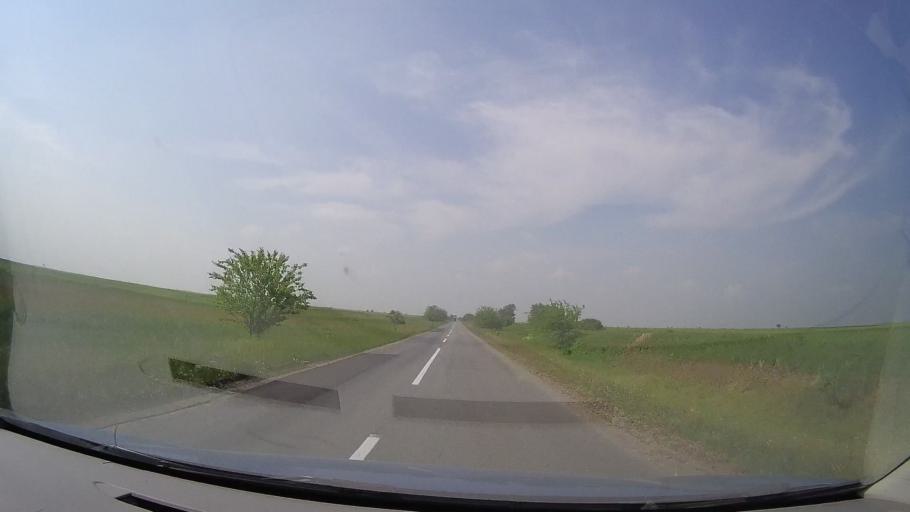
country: RS
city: Padina
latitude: 45.1593
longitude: 20.7494
